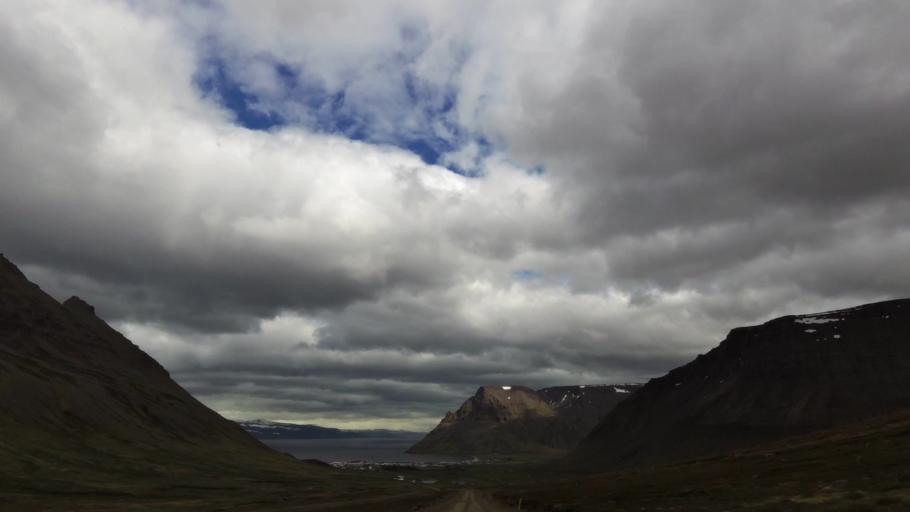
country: IS
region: Westfjords
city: Isafjoerdur
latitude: 66.1628
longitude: -23.3163
